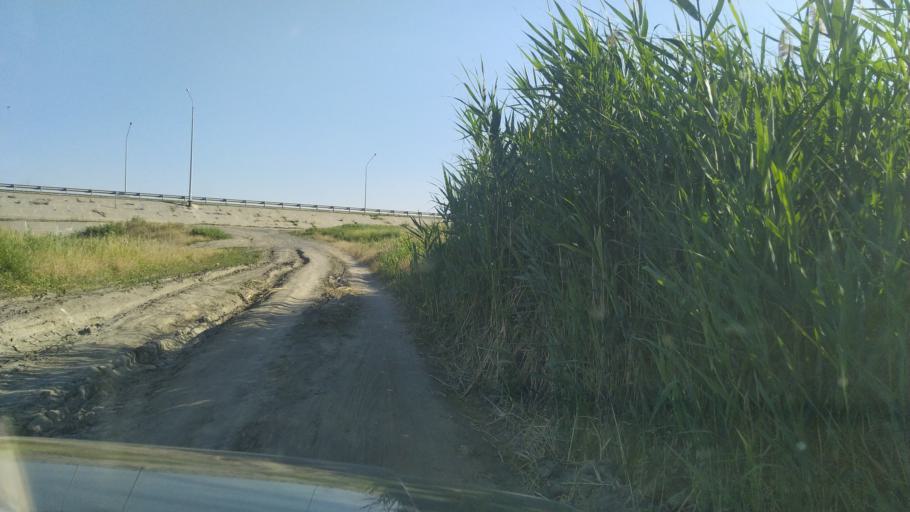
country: RU
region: Rostov
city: Kuleshovka
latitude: 47.1188
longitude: 39.6497
